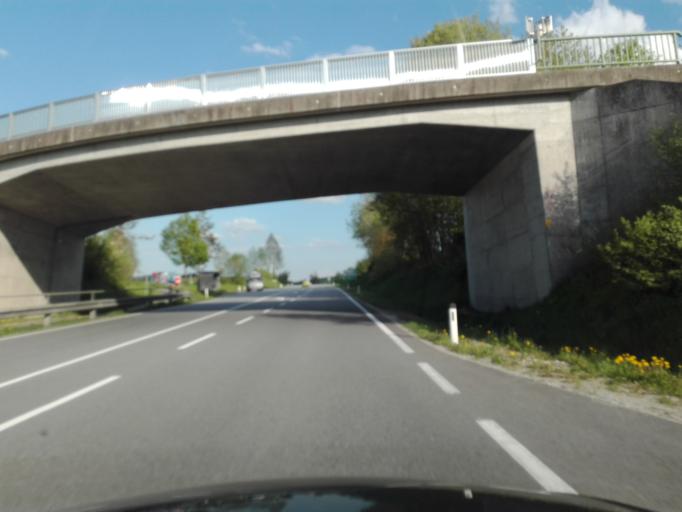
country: AT
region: Upper Austria
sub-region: Politischer Bezirk Rohrbach
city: Kleinzell im Muehlkreis
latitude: 48.4726
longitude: 14.0037
